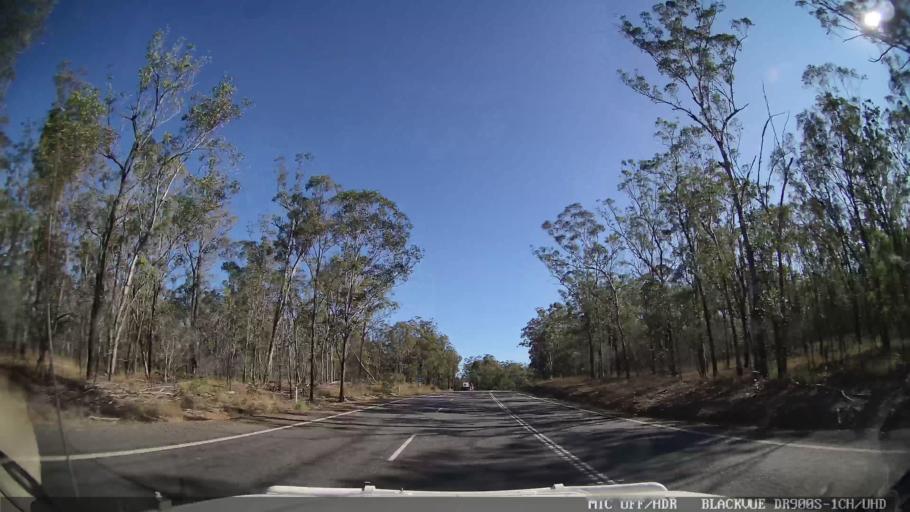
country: AU
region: Queensland
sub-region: Bundaberg
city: Childers
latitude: -25.2148
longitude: 152.0792
